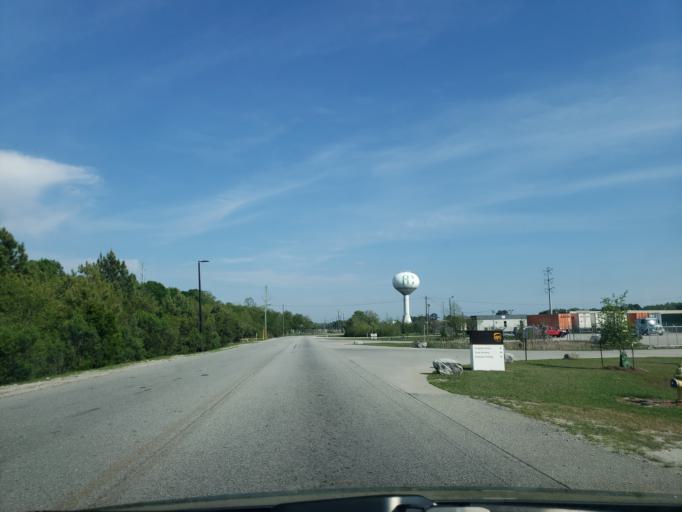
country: US
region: Georgia
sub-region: Chatham County
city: Garden City
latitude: 32.1018
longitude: -81.1856
